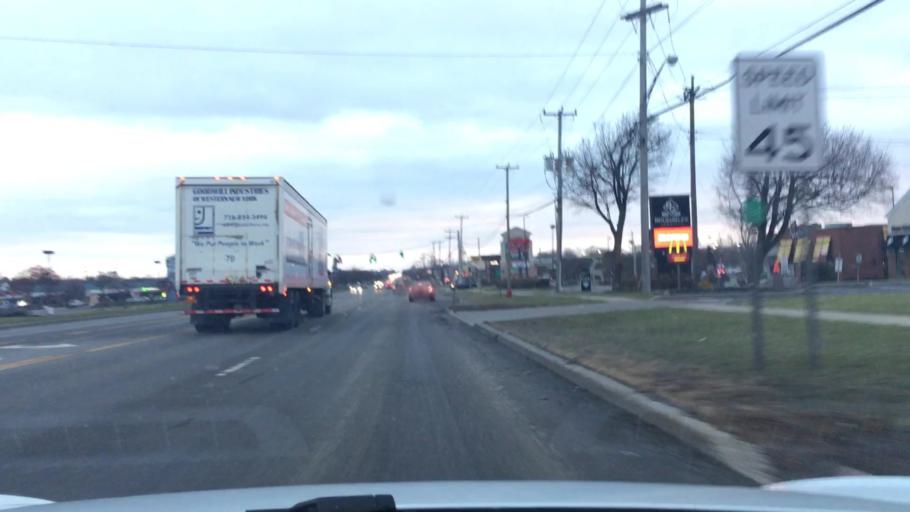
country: US
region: New York
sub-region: Erie County
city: Harris Hill
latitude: 42.9831
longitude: -78.6972
